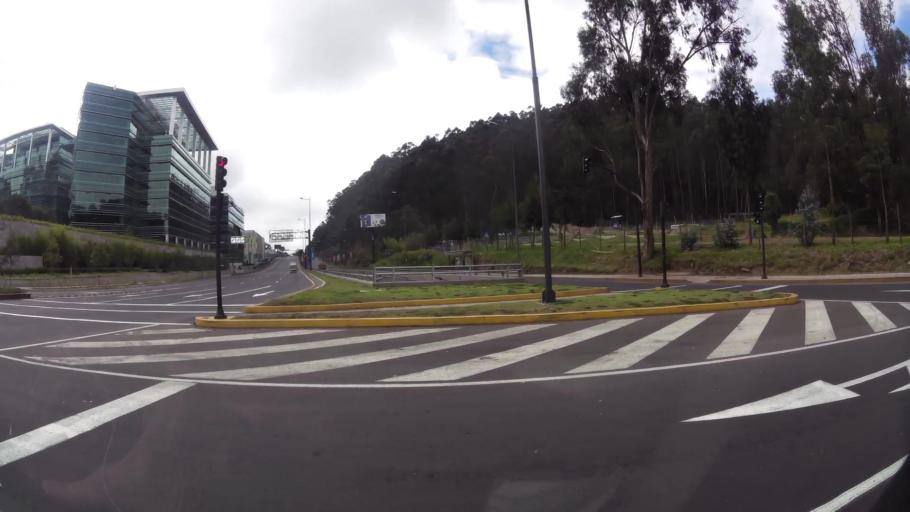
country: EC
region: Pichincha
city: Quito
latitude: -0.1631
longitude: -78.4626
